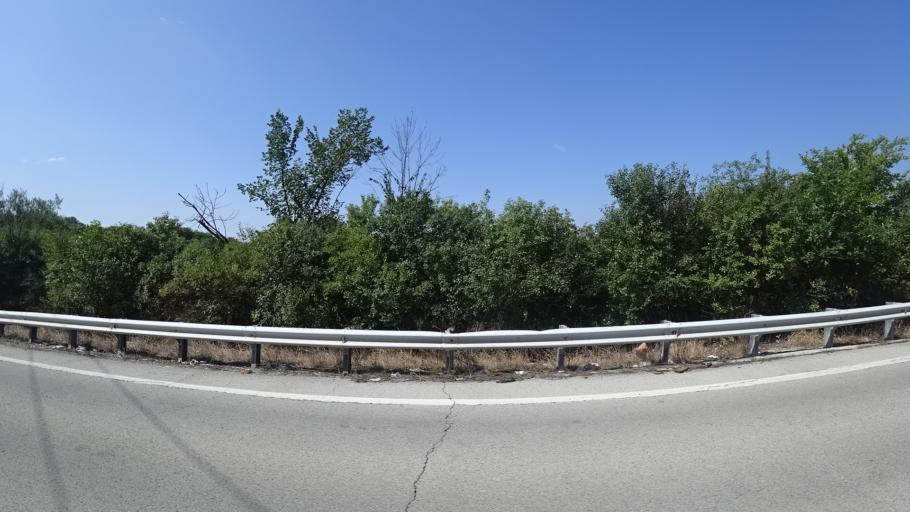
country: US
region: Illinois
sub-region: Cook County
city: Tinley Park
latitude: 41.5682
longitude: -87.7528
